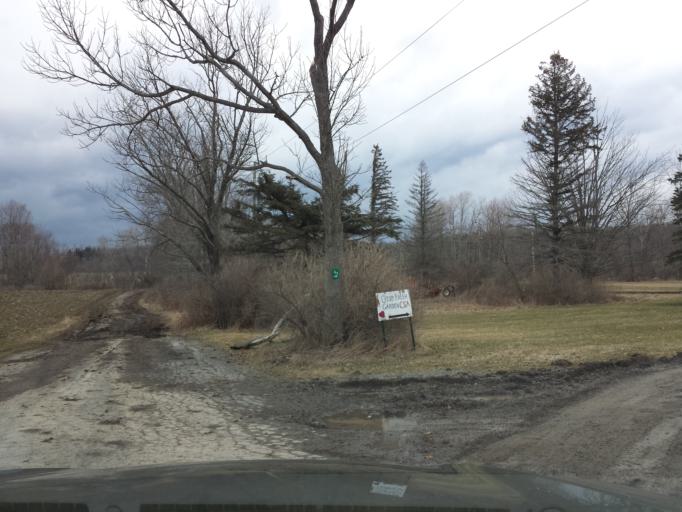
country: US
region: New York
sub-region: Tompkins County
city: Dryden
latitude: 42.3961
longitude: -76.3424
